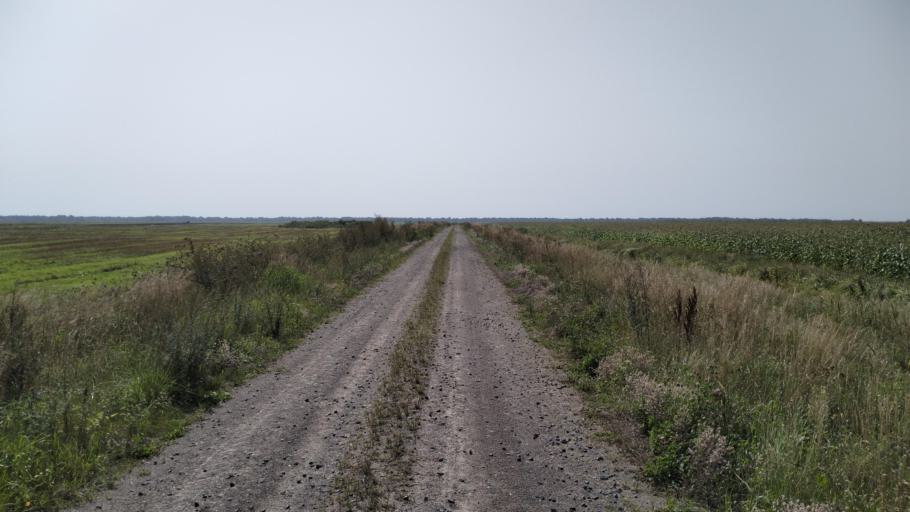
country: BY
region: Brest
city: Davyd-Haradok
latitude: 51.9911
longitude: 27.1644
